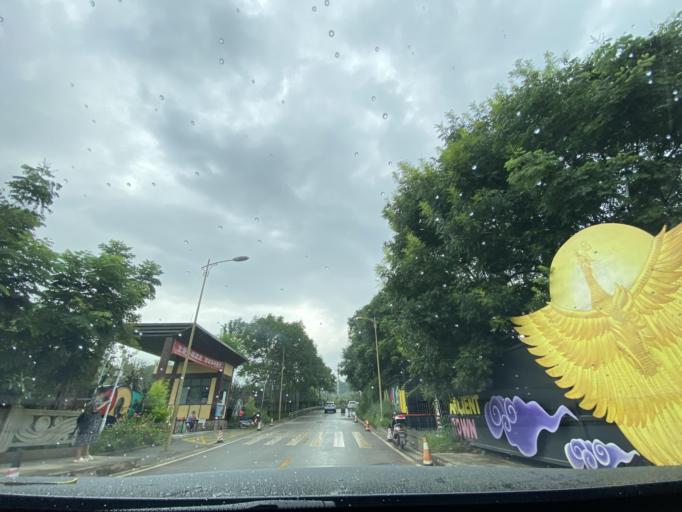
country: CN
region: Sichuan
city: Longquan
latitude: 30.6076
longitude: 104.4824
